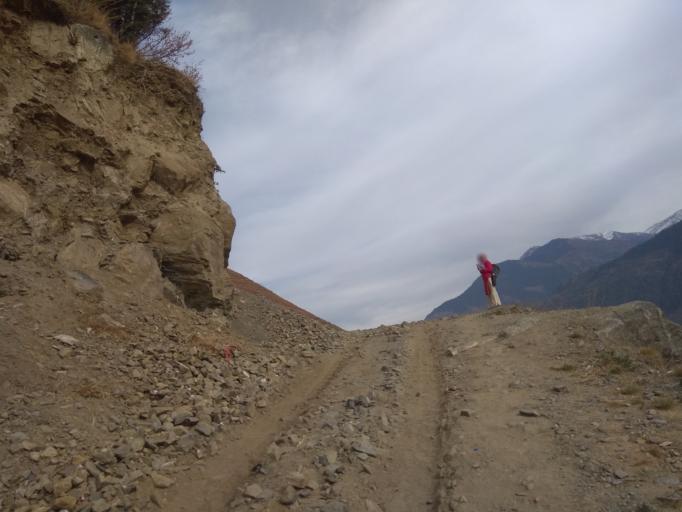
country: NP
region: Mid Western
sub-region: Bheri Zone
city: Dailekh
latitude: 29.2453
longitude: 81.6647
